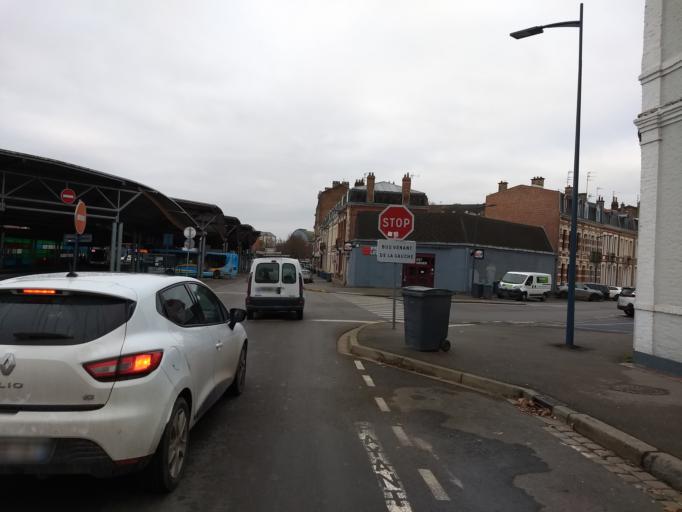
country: FR
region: Nord-Pas-de-Calais
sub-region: Departement du Pas-de-Calais
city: Arras
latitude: 50.2883
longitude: 2.7836
